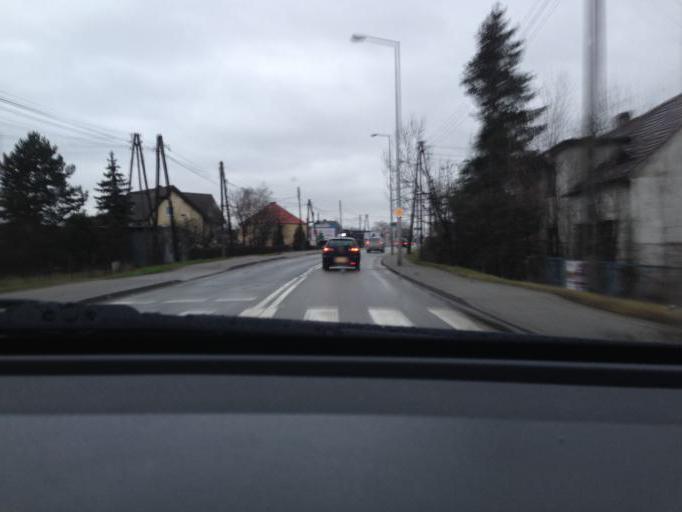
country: PL
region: Opole Voivodeship
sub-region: Powiat opolski
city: Opole
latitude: 50.6928
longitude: 17.9534
